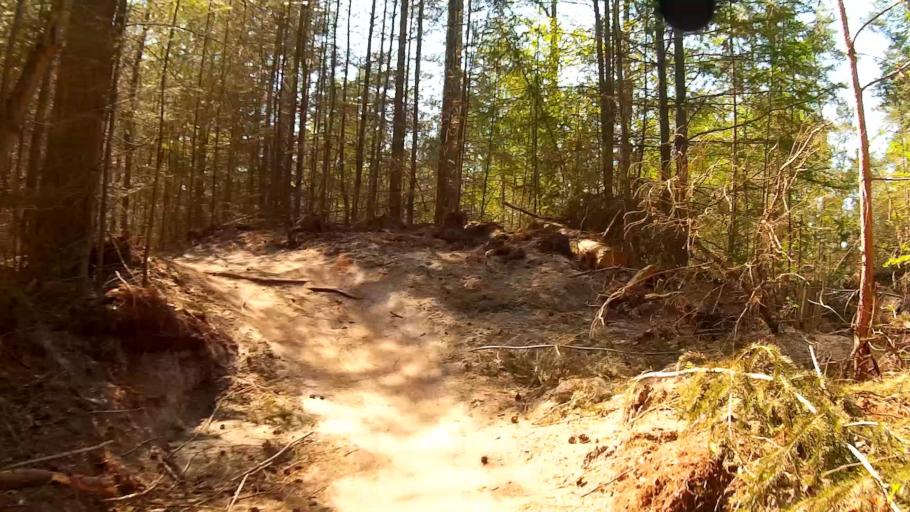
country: NL
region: Utrecht
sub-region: Gemeente Baarn
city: Baarn
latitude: 52.1984
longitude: 5.2691
